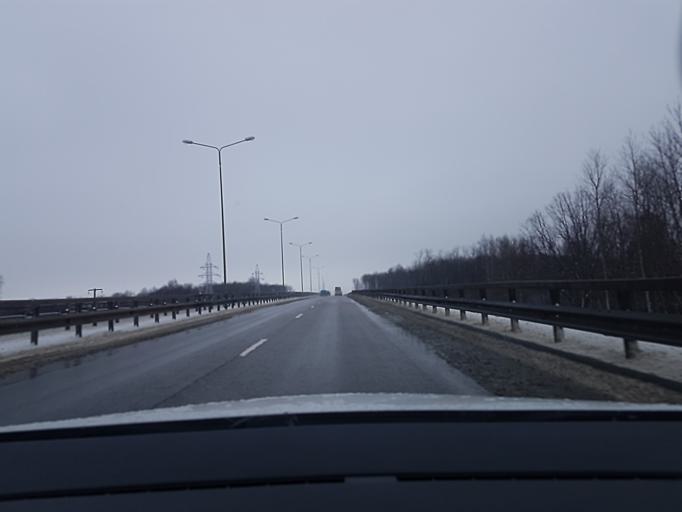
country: RU
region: Moskovskaya
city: Ozherel'ye
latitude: 54.7470
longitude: 38.2312
